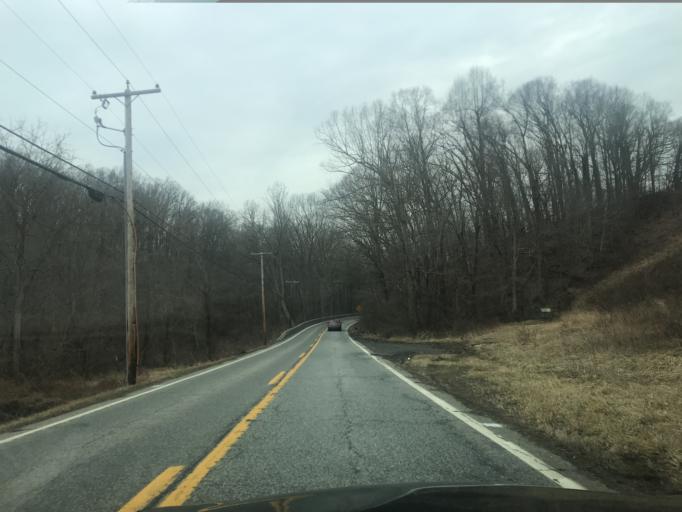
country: US
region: Maryland
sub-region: Harford County
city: Bel Air North
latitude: 39.6116
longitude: -76.3999
